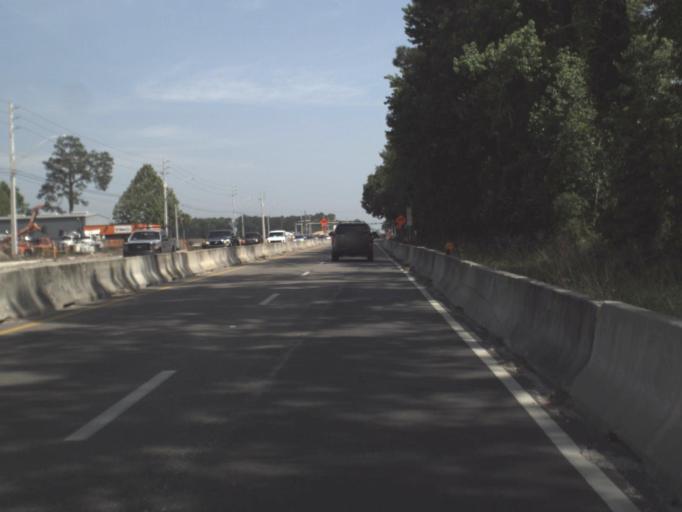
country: US
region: Florida
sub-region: Saint Johns County
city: Fruit Cove
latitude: 30.1400
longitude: -81.5148
